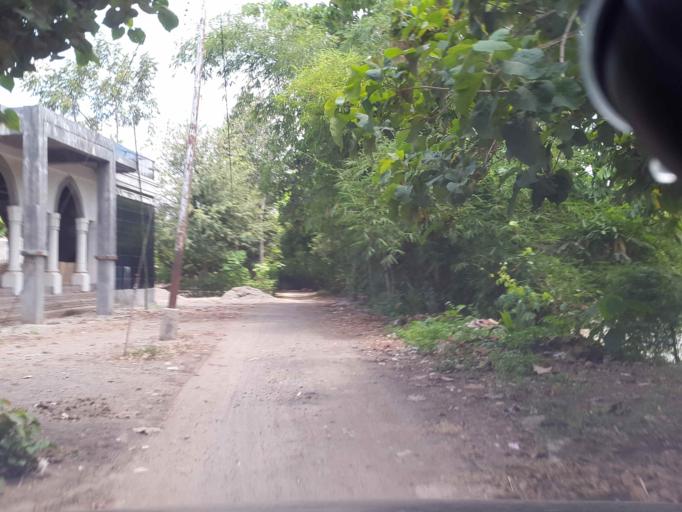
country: ID
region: West Nusa Tenggara
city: Jelateng Timur
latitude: -8.6952
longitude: 116.0920
